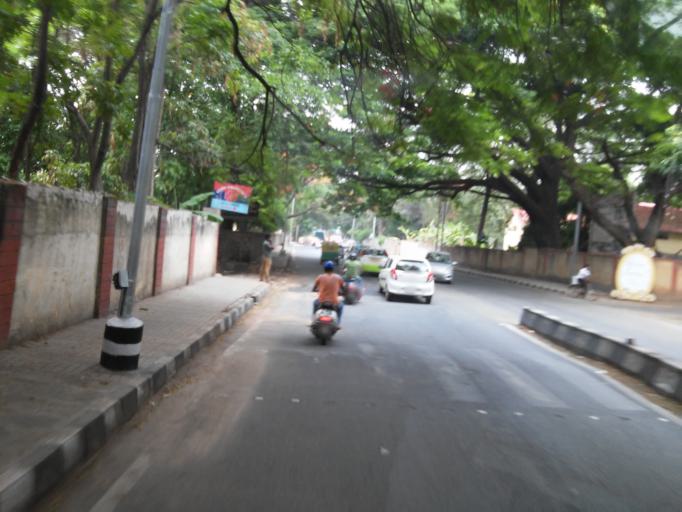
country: IN
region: Karnataka
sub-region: Bangalore Urban
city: Bangalore
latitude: 12.9897
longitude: 77.6156
